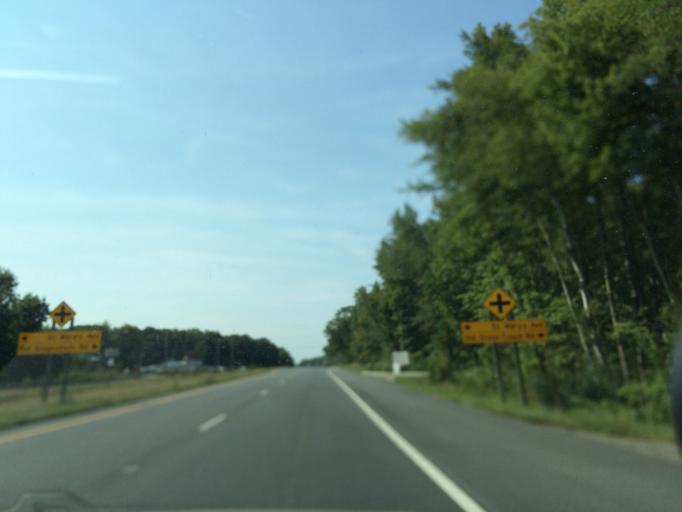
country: US
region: Maryland
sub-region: Charles County
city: La Plata
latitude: 38.5069
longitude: -76.9845
